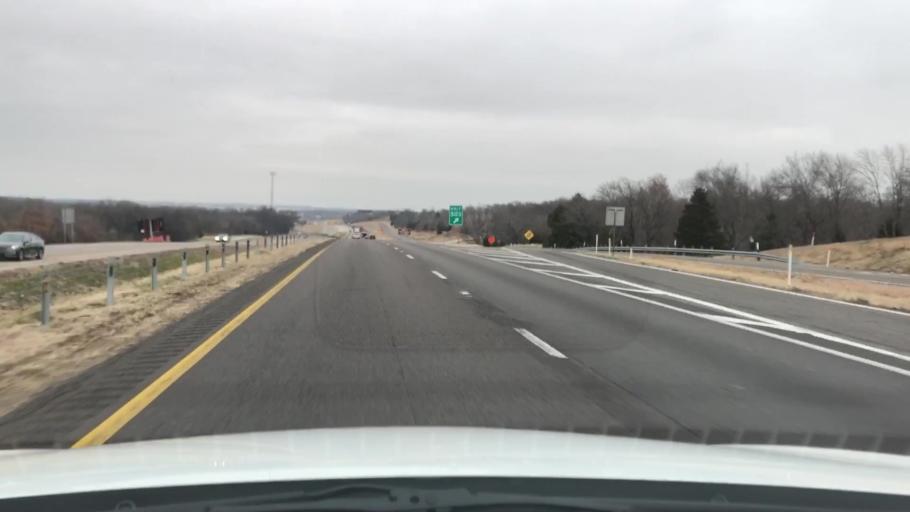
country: US
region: Texas
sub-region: Cooke County
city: Gainesville
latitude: 33.7116
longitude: -97.1614
